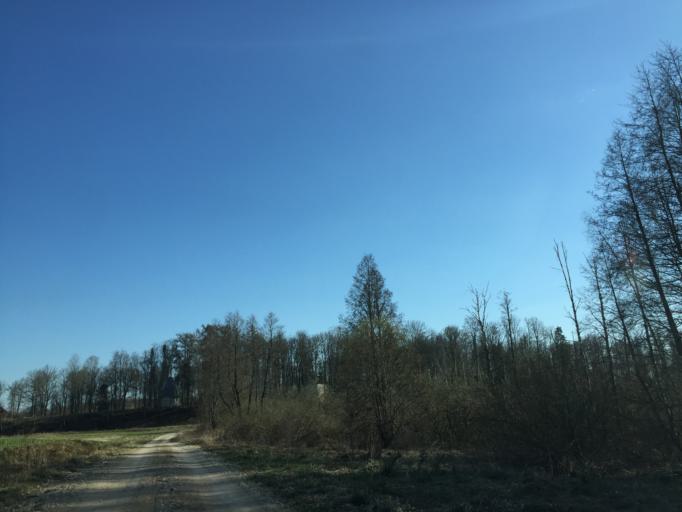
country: EE
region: Valgamaa
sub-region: Torva linn
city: Torva
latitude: 58.2380
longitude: 25.9006
